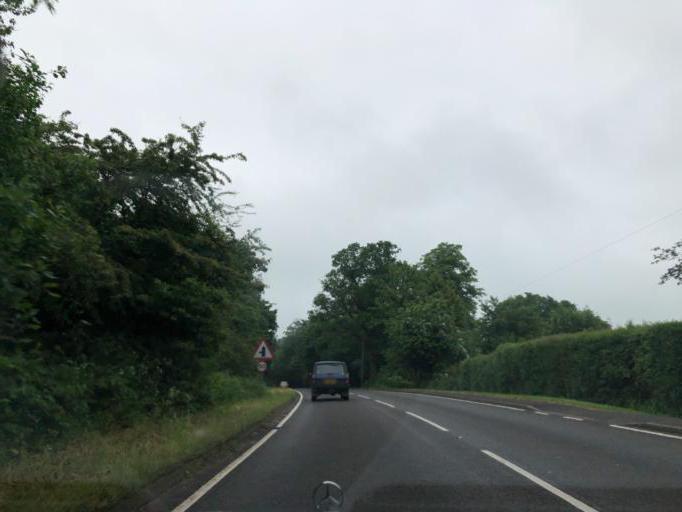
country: GB
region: England
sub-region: Warwickshire
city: Wroxall
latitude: 52.3210
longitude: -1.6664
